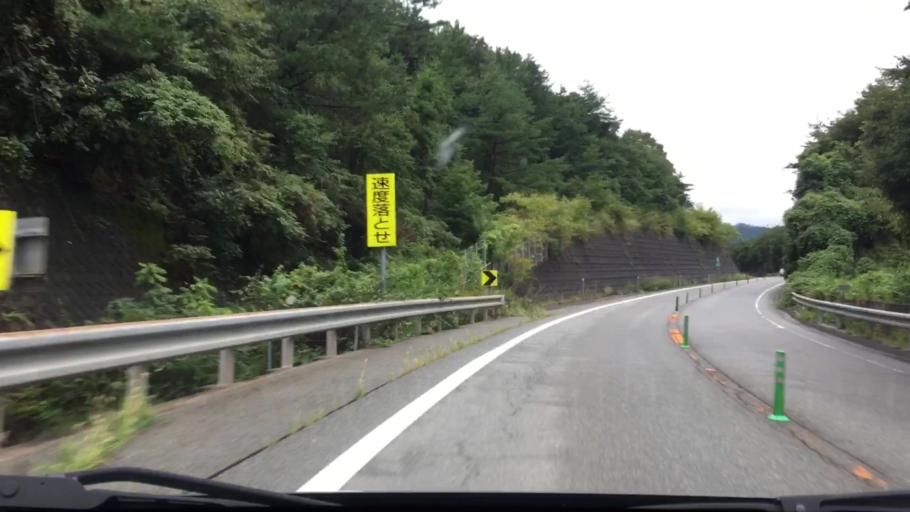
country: JP
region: Hyogo
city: Nishiwaki
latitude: 35.0341
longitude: 134.7690
